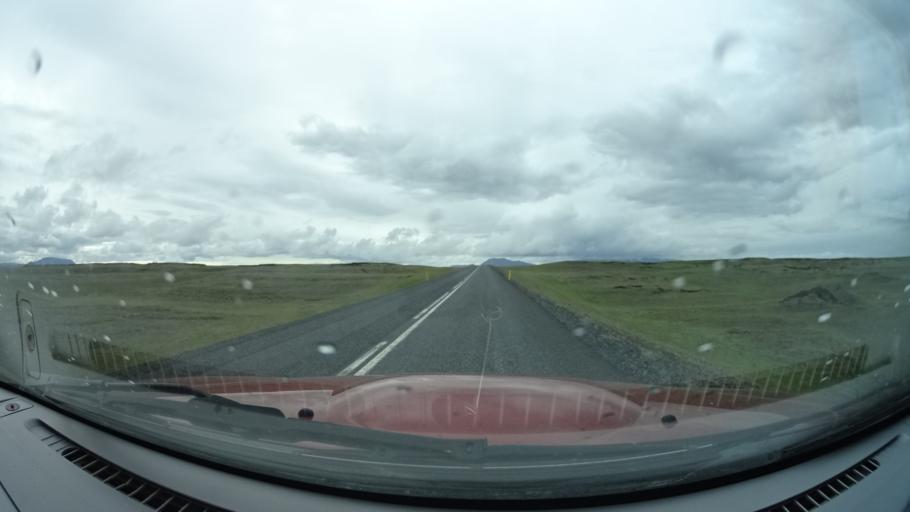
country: IS
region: Northeast
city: Laugar
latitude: 65.6510
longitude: -16.3902
